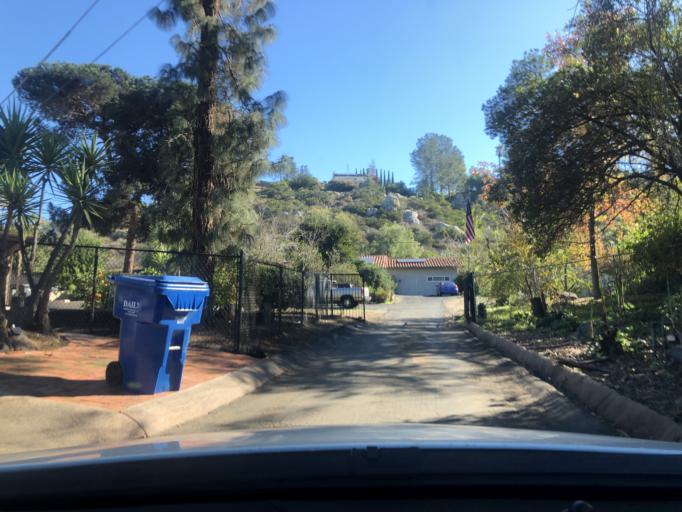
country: US
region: California
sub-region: San Diego County
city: El Cajon
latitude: 32.7825
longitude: -116.9436
